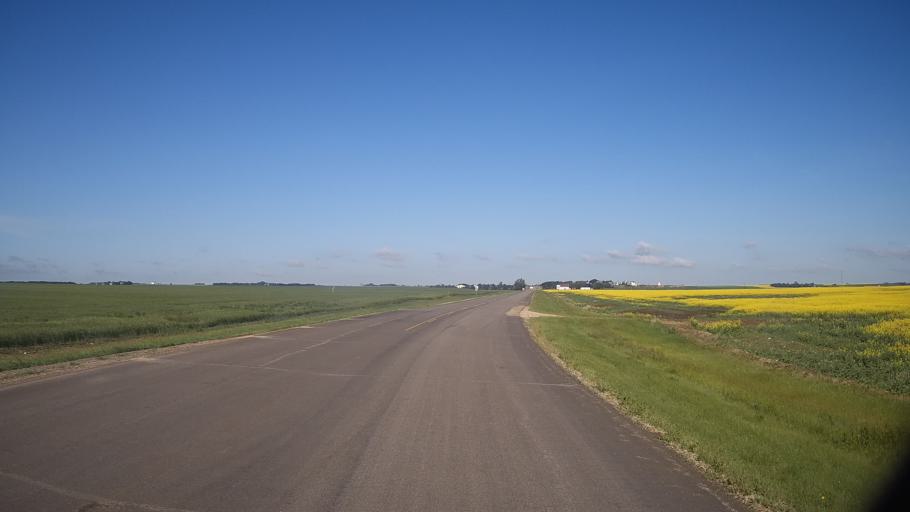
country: CA
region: Saskatchewan
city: Watrous
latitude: 51.6781
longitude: -105.3857
